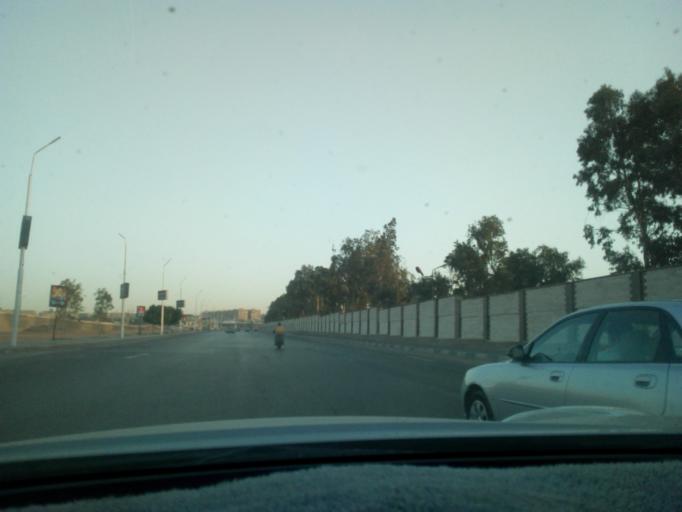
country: EG
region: Muhafazat al Qalyubiyah
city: Al Khankah
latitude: 30.1154
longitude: 31.3654
